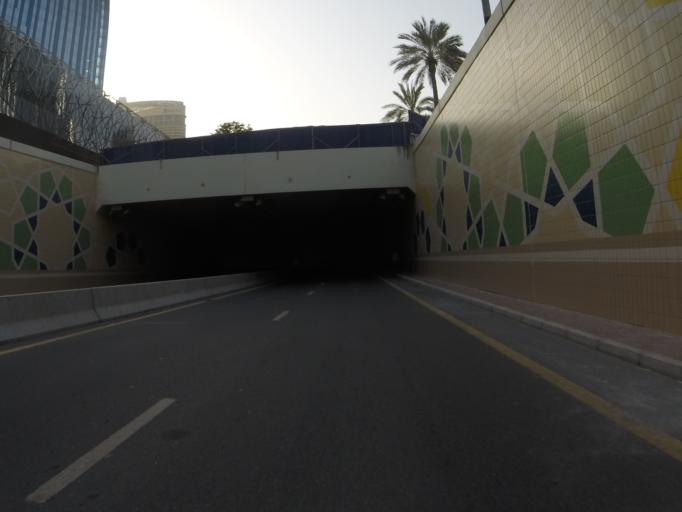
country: AE
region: Dubai
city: Dubai
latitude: 25.1994
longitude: 55.2723
